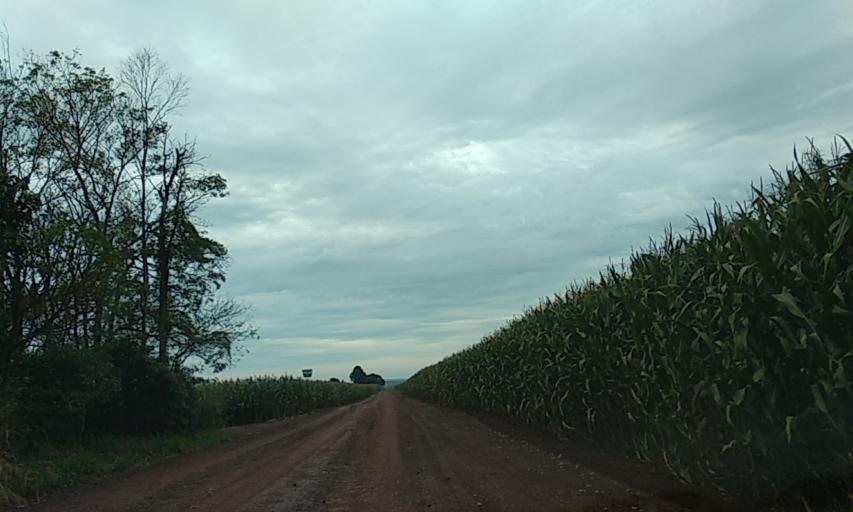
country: BR
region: Parana
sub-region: Marechal Candido Rondon
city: Marechal Candido Rondon
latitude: -24.5401
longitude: -54.0941
